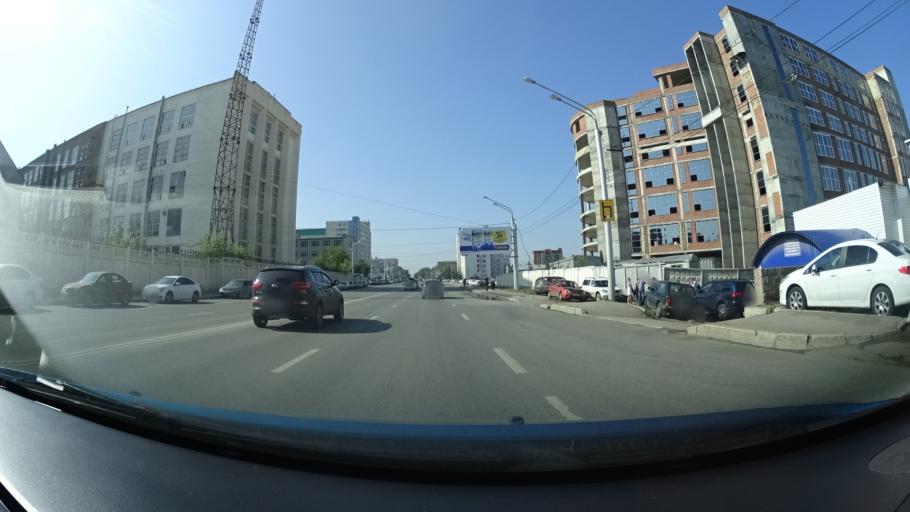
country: RU
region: Bashkortostan
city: Ufa
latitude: 54.7441
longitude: 55.9686
